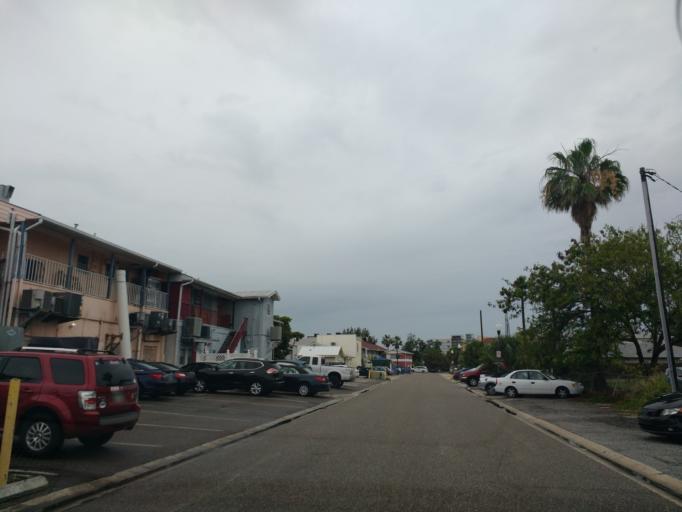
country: US
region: Florida
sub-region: Pinellas County
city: Madeira Beach
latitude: 27.7868
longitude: -82.7831
